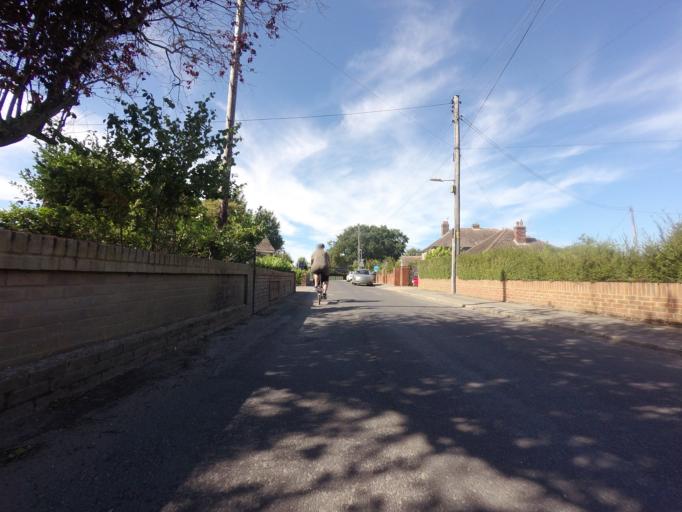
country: GB
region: England
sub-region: Kent
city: Birchington-on-Sea
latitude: 51.3519
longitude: 1.2544
